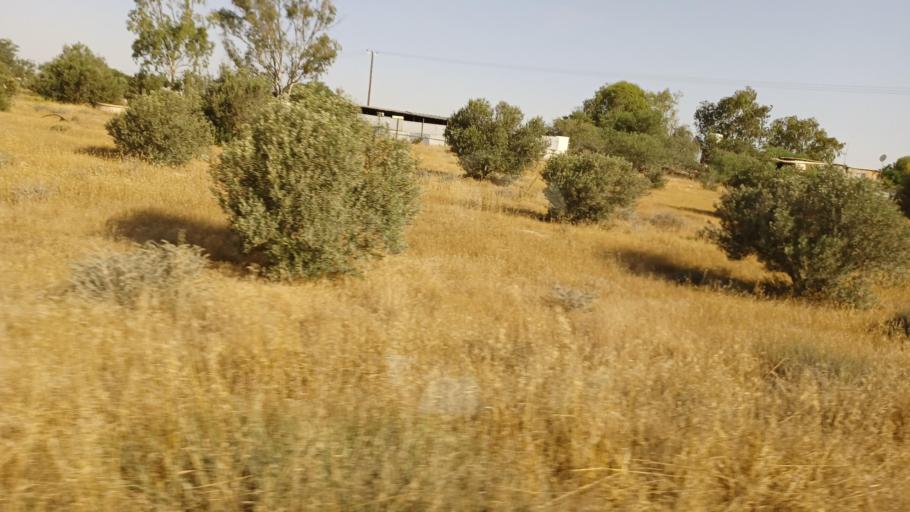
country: CY
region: Ammochostos
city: Liopetri
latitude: 34.9930
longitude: 33.8831
